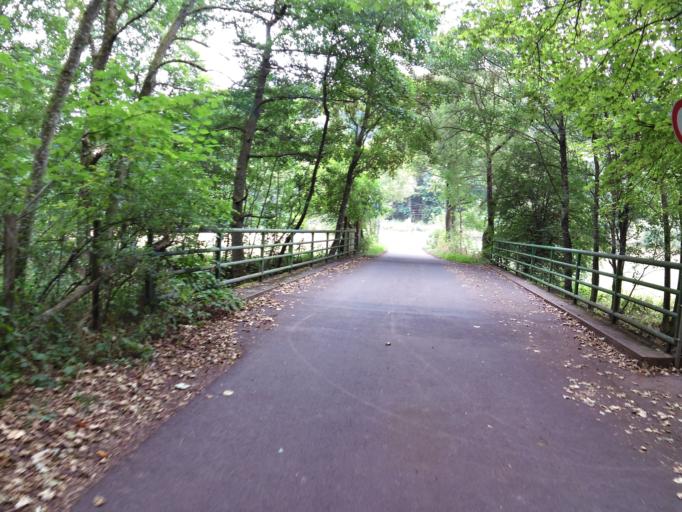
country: DE
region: North Rhine-Westphalia
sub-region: Regierungsbezirk Koln
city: Nettersheim
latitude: 50.5118
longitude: 6.5870
